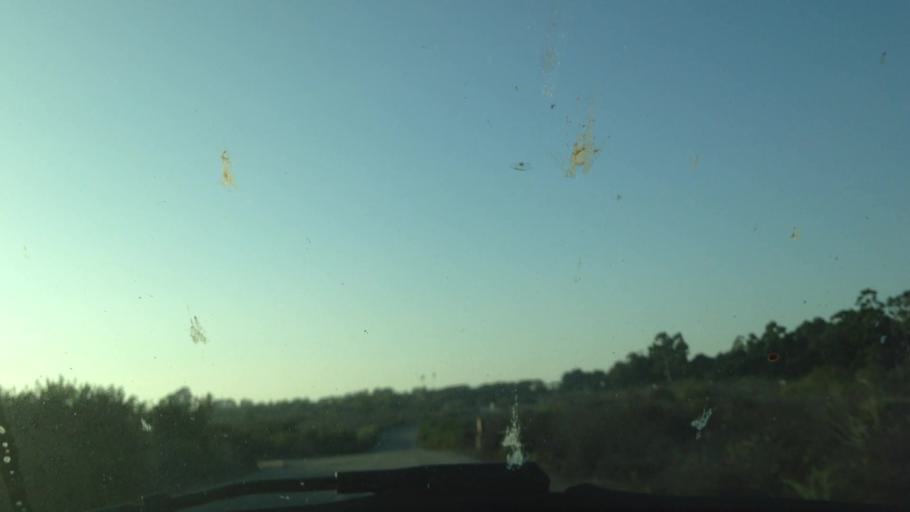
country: US
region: California
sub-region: Orange County
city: San Joaquin Hills
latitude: 33.5823
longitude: -117.8508
